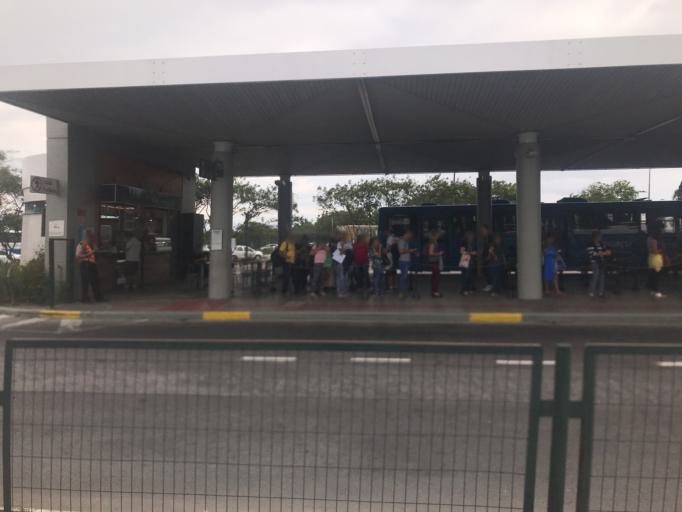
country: BR
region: Santa Catarina
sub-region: Florianopolis
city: Florianopolis
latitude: -27.5993
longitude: -48.5535
